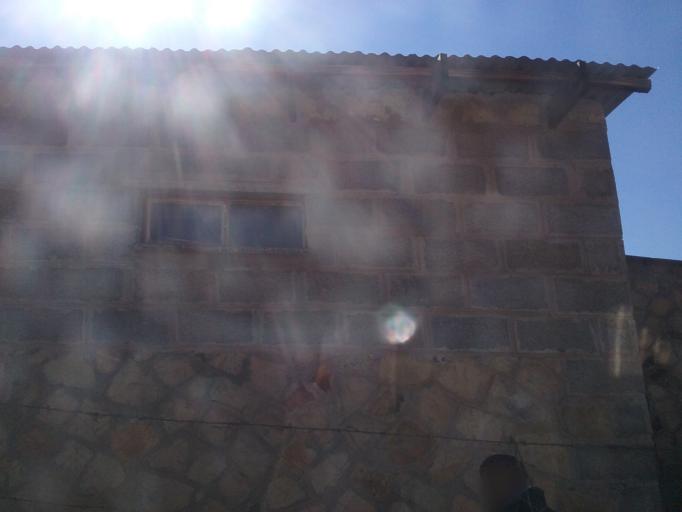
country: LS
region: Maseru
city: Maseru
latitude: -29.4439
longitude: 27.5702
